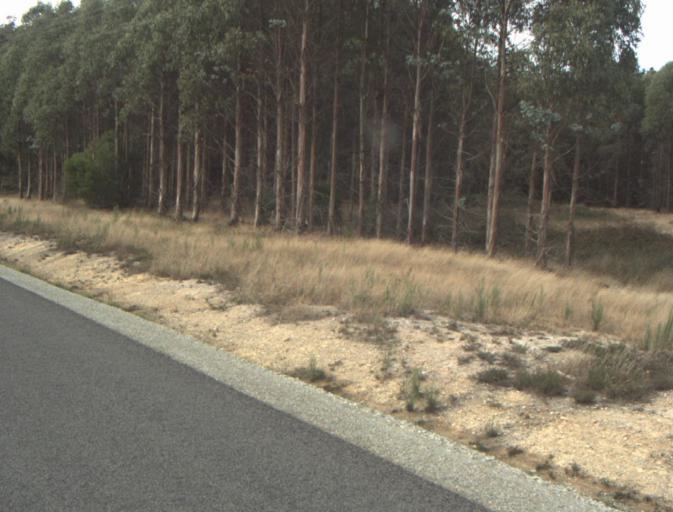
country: AU
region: Tasmania
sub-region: Launceston
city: Mayfield
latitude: -41.1968
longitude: 147.1810
